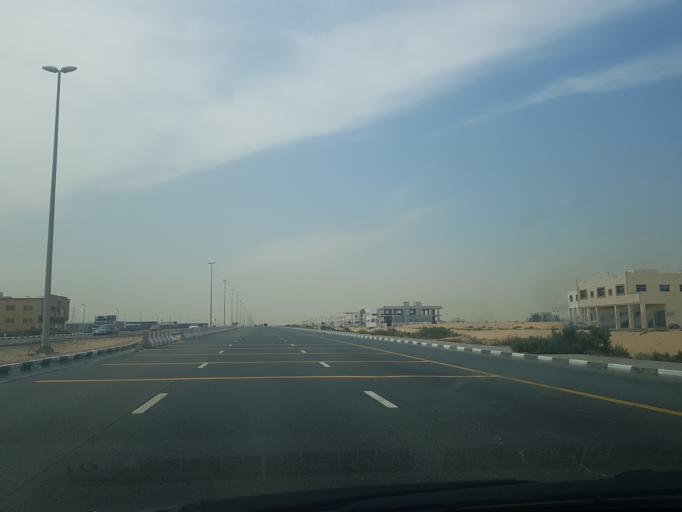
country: AE
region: Ash Shariqah
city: Sharjah
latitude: 25.2492
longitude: 55.5379
